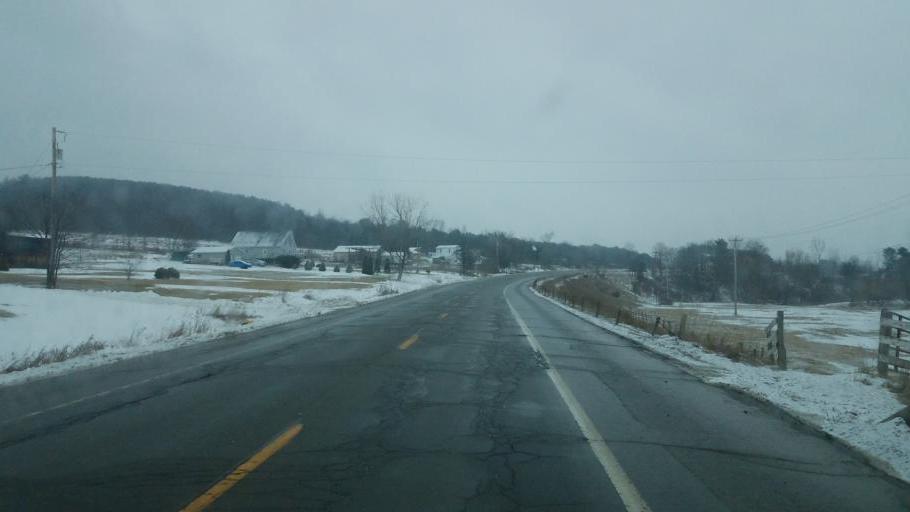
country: US
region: Pennsylvania
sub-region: Tioga County
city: Westfield
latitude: 42.1092
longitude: -77.4777
